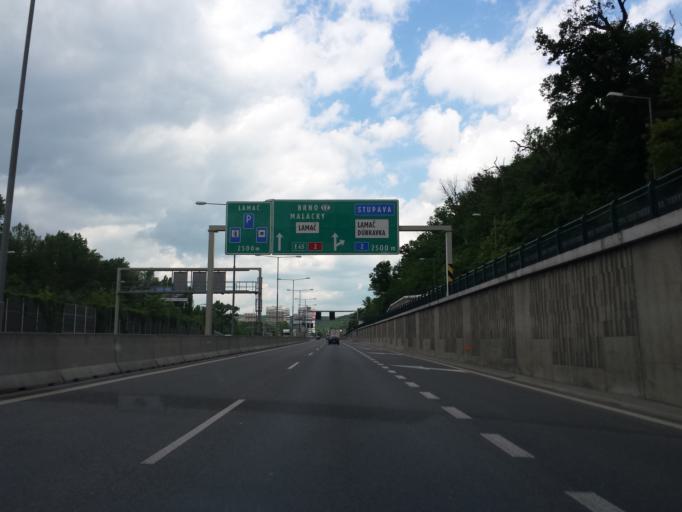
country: SK
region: Bratislavsky
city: Bratislava
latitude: 48.1578
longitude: 17.0764
